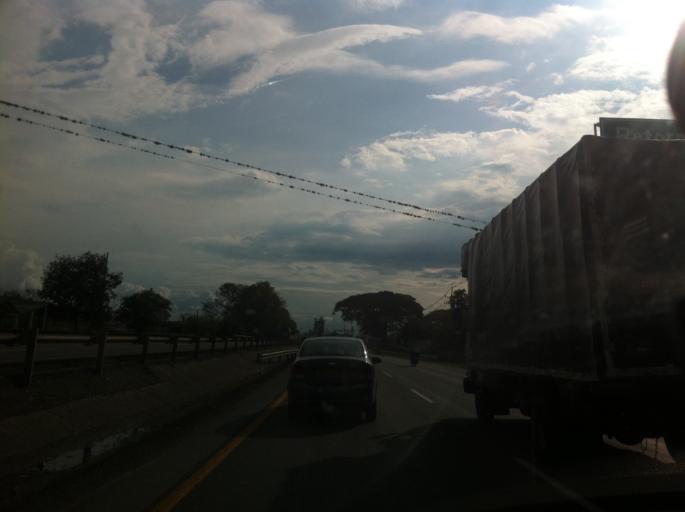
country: CO
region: Valle del Cauca
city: Buga
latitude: 3.9419
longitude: -76.2793
